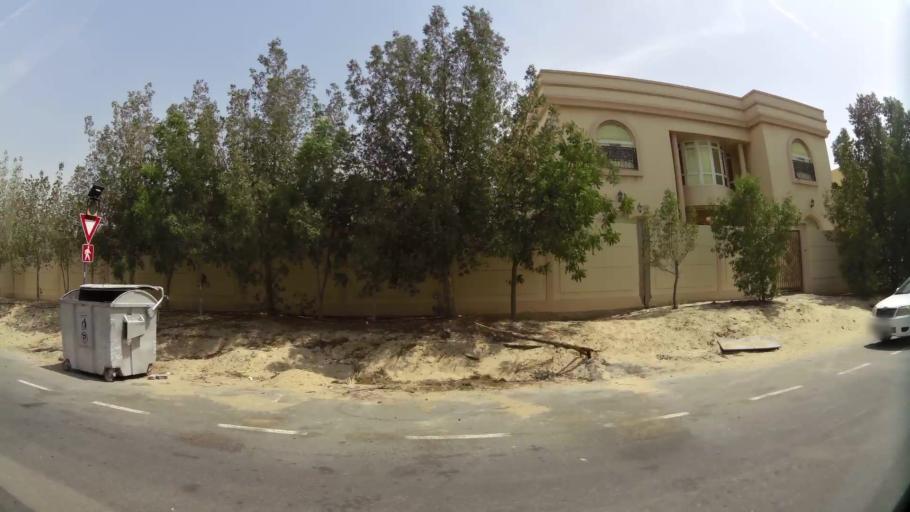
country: AE
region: Ash Shariqah
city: Sharjah
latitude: 25.2588
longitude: 55.4766
